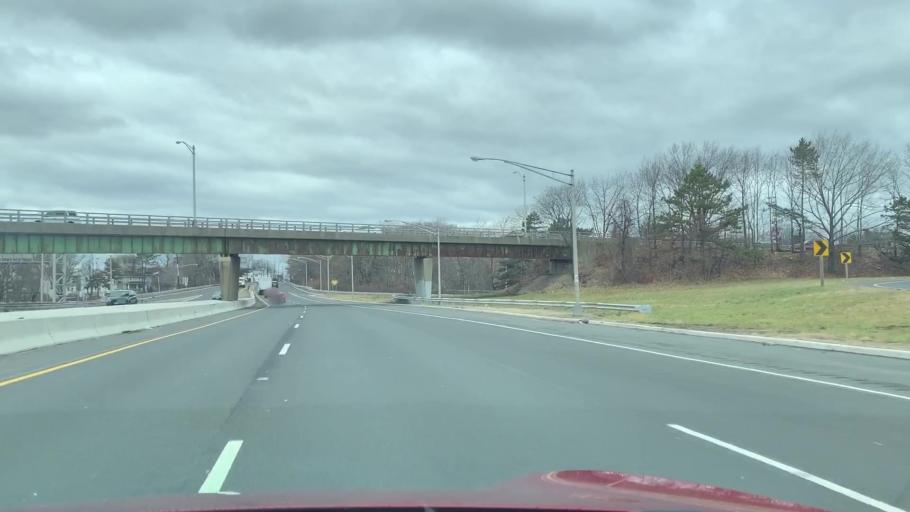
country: US
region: New Jersey
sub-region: Bergen County
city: Ridgefield Park
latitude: 40.8473
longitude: -74.0187
